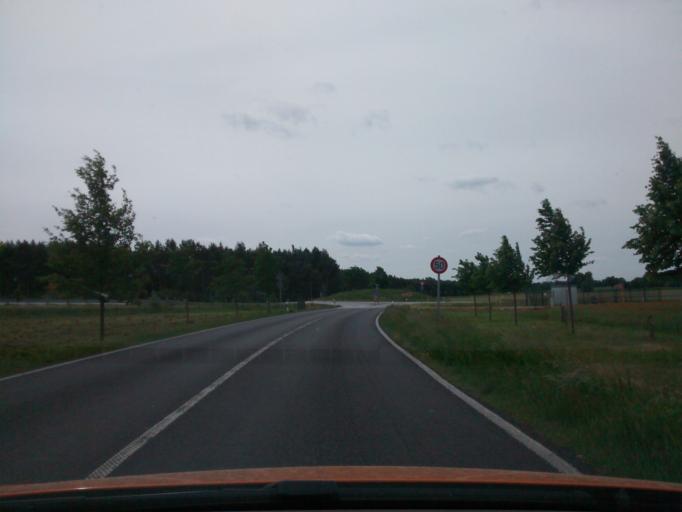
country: DE
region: Brandenburg
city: Trebbin
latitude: 52.2327
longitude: 13.2279
